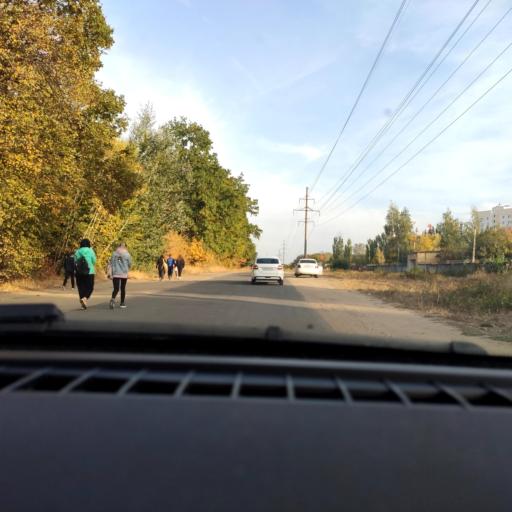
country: RU
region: Voronezj
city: Podgornoye
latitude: 51.7312
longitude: 39.2065
